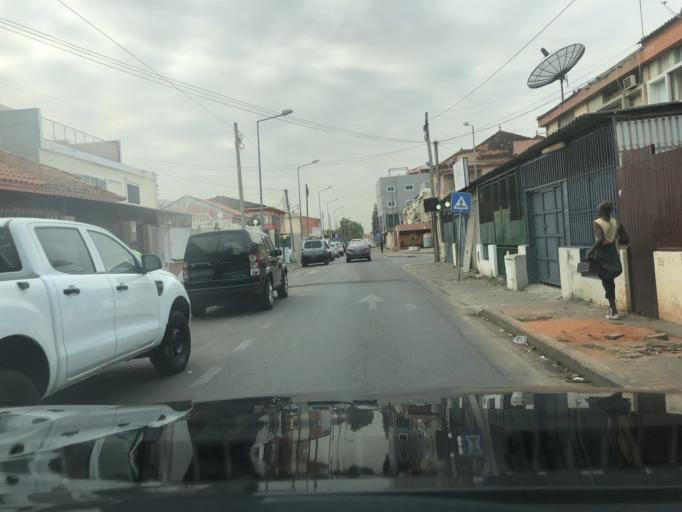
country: AO
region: Luanda
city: Luanda
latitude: -8.8253
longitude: 13.2503
